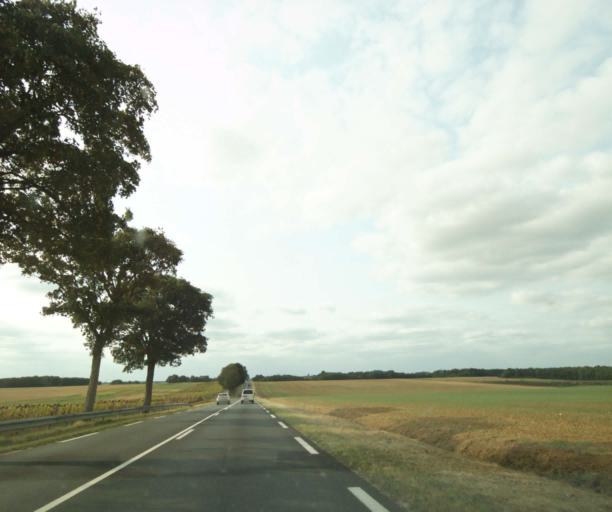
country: FR
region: Centre
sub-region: Departement d'Indre-et-Loire
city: Reignac-sur-Indre
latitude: 47.2260
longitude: 0.8813
